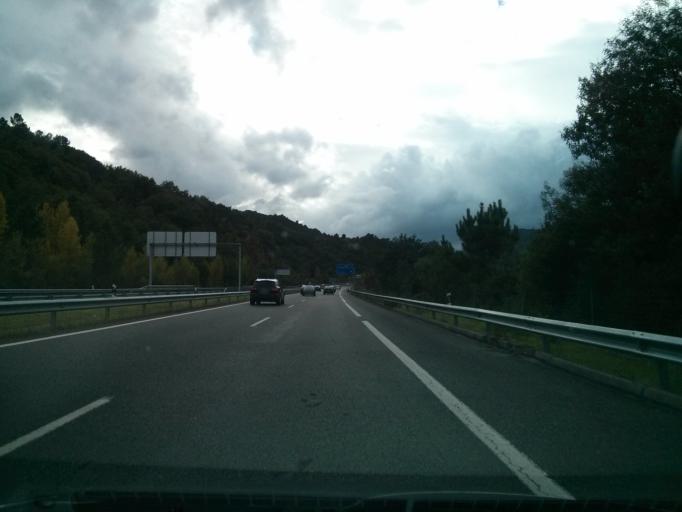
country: ES
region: Galicia
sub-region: Provincia de Ourense
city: Ourense
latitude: 42.3476
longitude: -7.8993
